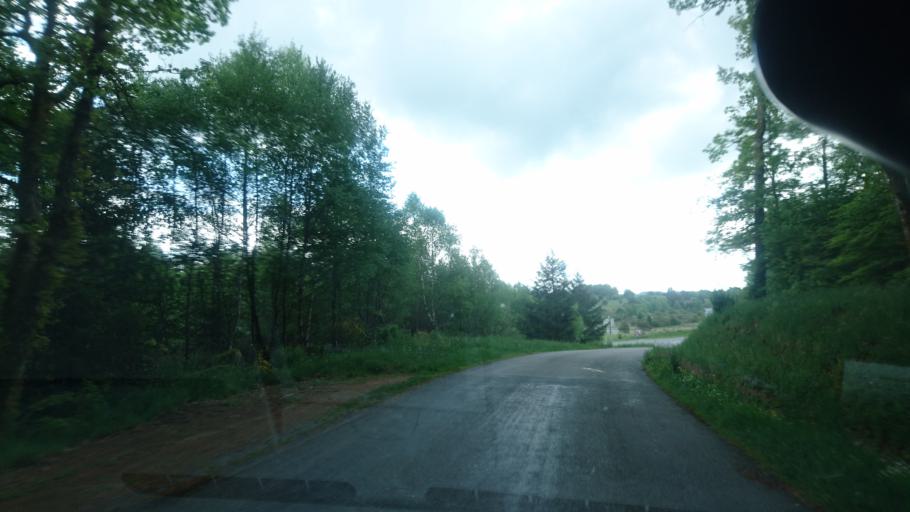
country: FR
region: Limousin
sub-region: Departement de la Haute-Vienne
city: Peyrat-le-Chateau
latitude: 45.7901
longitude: 1.9213
